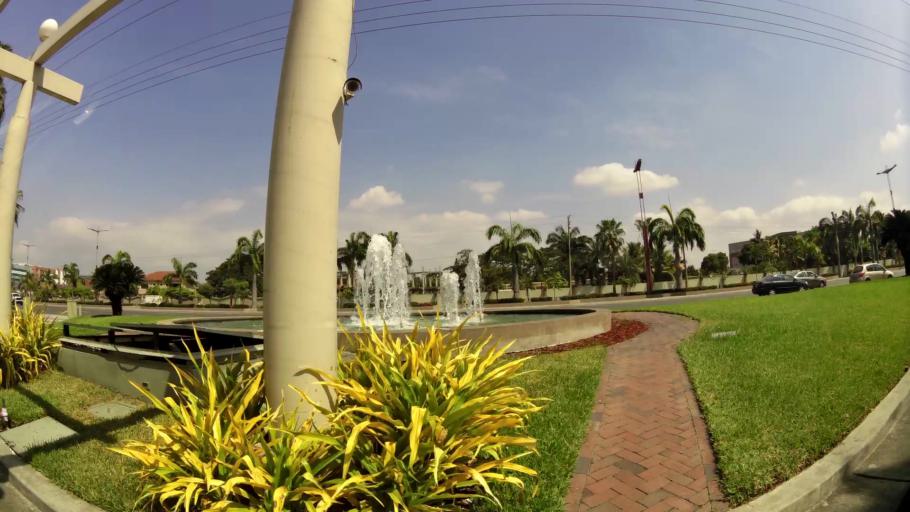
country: EC
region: Guayas
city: Eloy Alfaro
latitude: -2.1350
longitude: -79.8629
